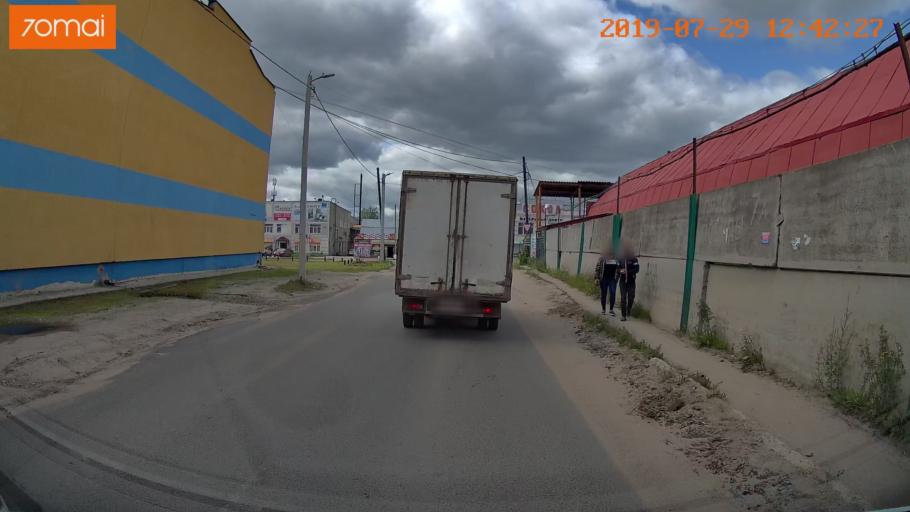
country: RU
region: Ivanovo
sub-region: Gorod Ivanovo
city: Ivanovo
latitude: 57.0057
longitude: 40.9314
